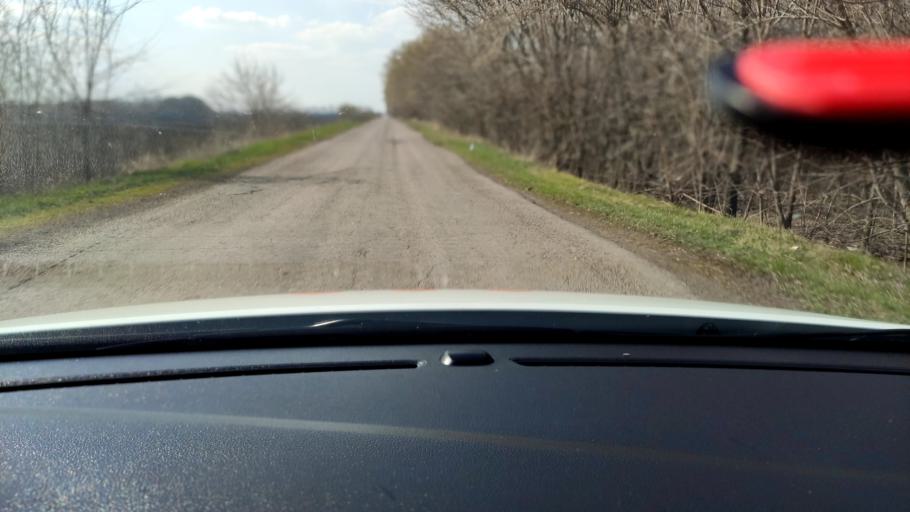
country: RU
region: Voronezj
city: Uryv-Pokrovka
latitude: 51.1241
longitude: 39.1210
